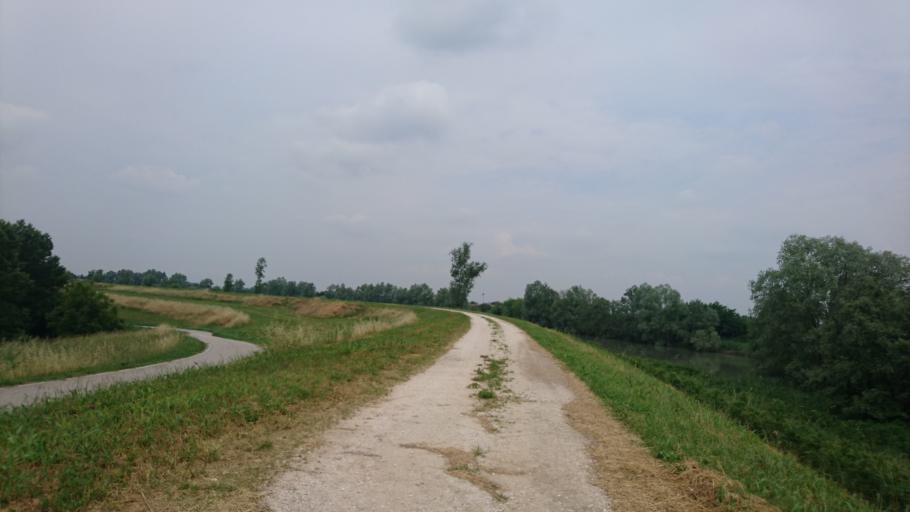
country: IT
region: Veneto
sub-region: Provincia di Padova
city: Piacenza d'Adige
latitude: 45.1216
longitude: 11.5800
